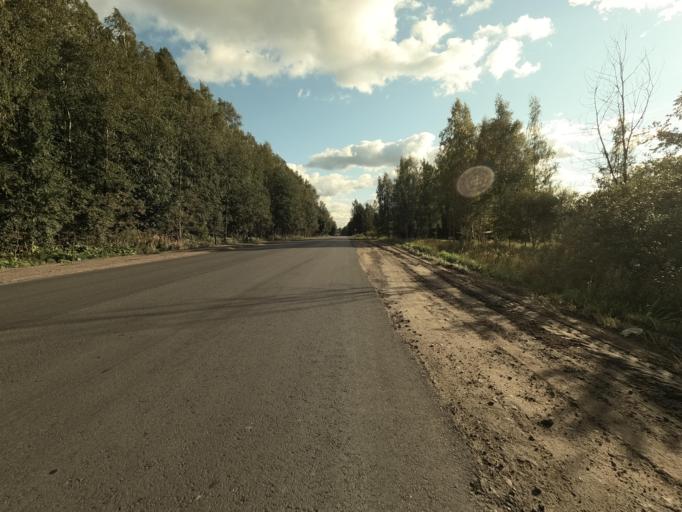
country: RU
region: Leningrad
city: Koltushi
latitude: 59.9298
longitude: 30.6642
